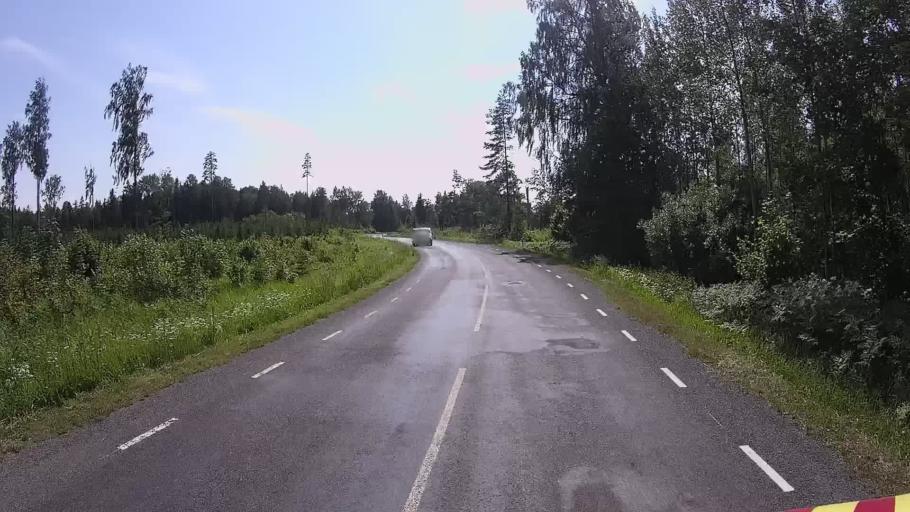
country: EE
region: Viljandimaa
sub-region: Karksi vald
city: Karksi-Nuia
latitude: 58.0333
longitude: 25.5432
